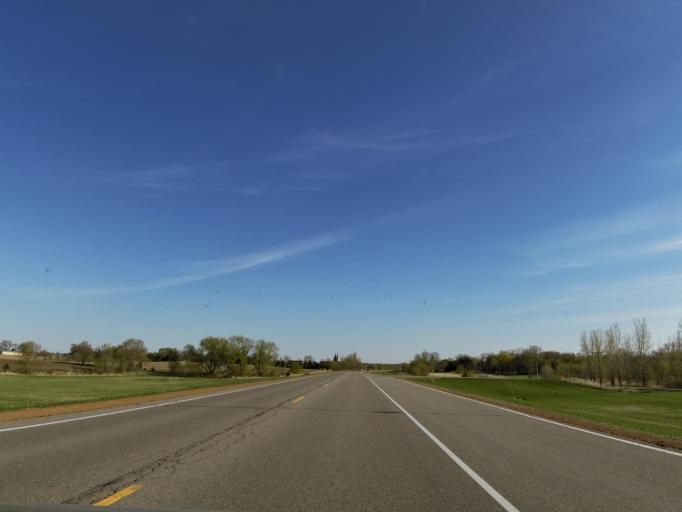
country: US
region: Minnesota
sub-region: Scott County
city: Prior Lake
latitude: 44.6581
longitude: -93.5007
